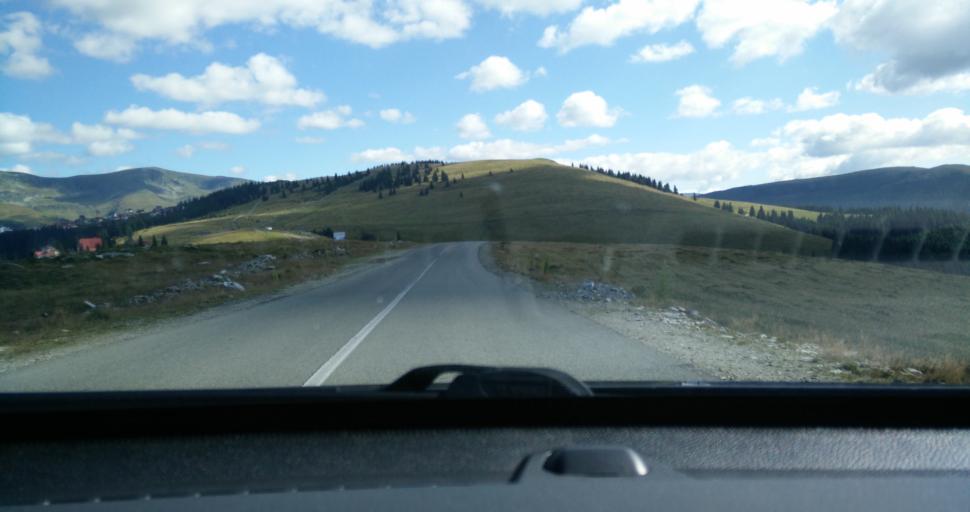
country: RO
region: Gorj
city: Novaci-Straini
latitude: 45.2712
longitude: 23.6862
